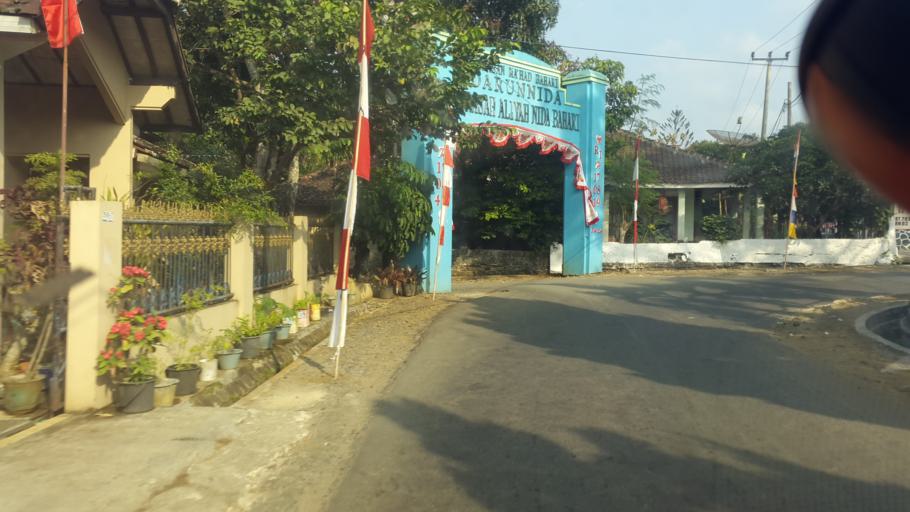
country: ID
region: West Java
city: Jampang Kulon
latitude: -7.2598
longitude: 106.6256
